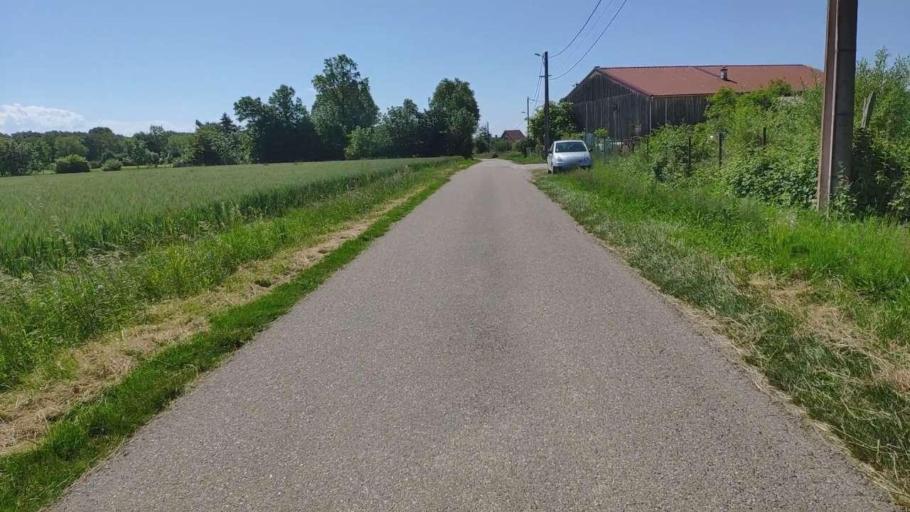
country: FR
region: Franche-Comte
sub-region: Departement du Jura
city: Bletterans
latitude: 46.7683
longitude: 5.4084
